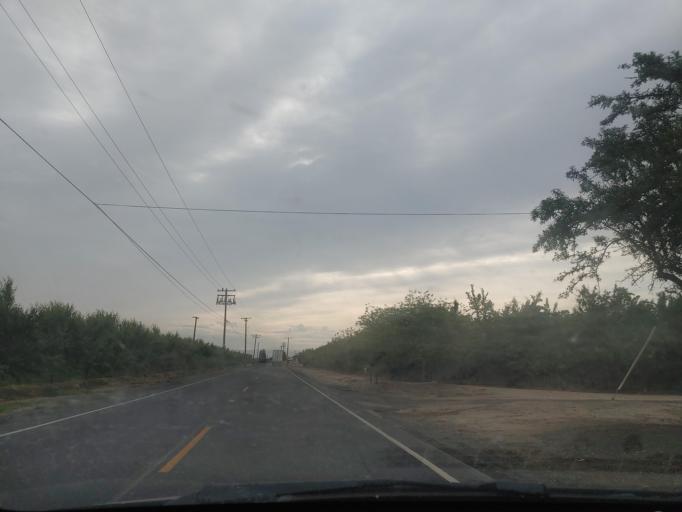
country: US
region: California
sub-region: Stanislaus County
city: Salida
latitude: 37.6815
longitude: -121.1163
